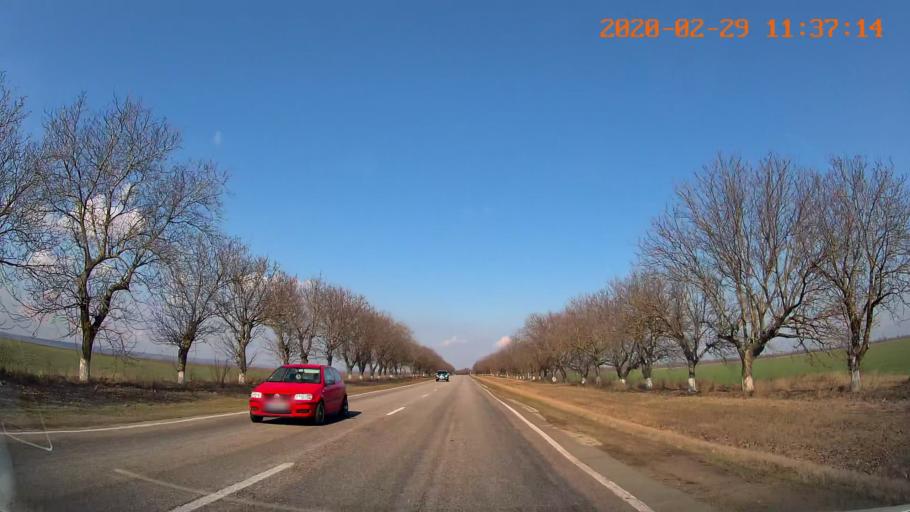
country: MD
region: Rezina
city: Saharna
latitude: 47.6086
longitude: 29.0479
